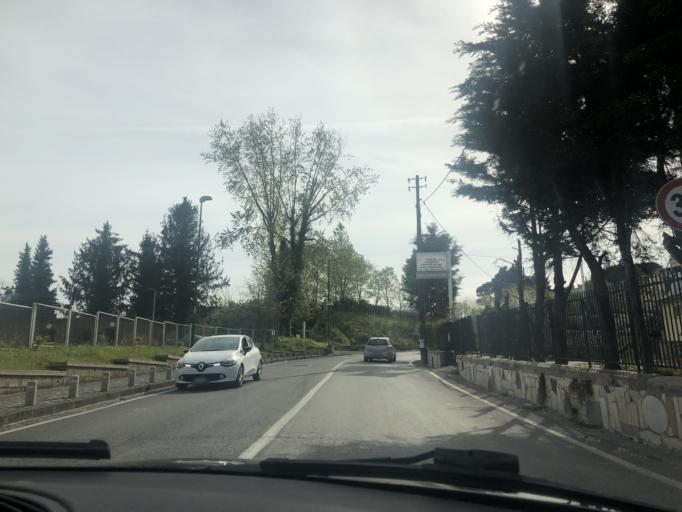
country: IT
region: Campania
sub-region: Provincia di Napoli
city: Torre Caracciolo
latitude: 40.8677
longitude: 14.2037
